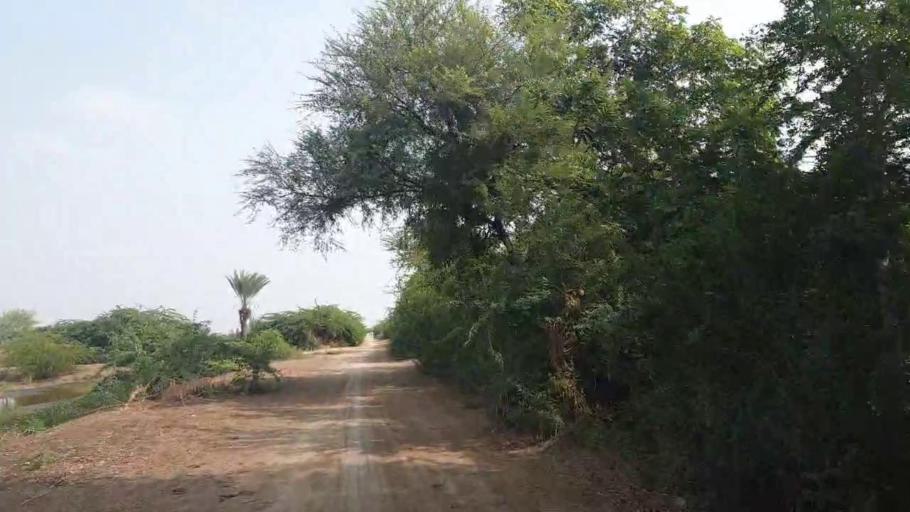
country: PK
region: Sindh
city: Badin
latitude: 24.5475
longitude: 68.7147
